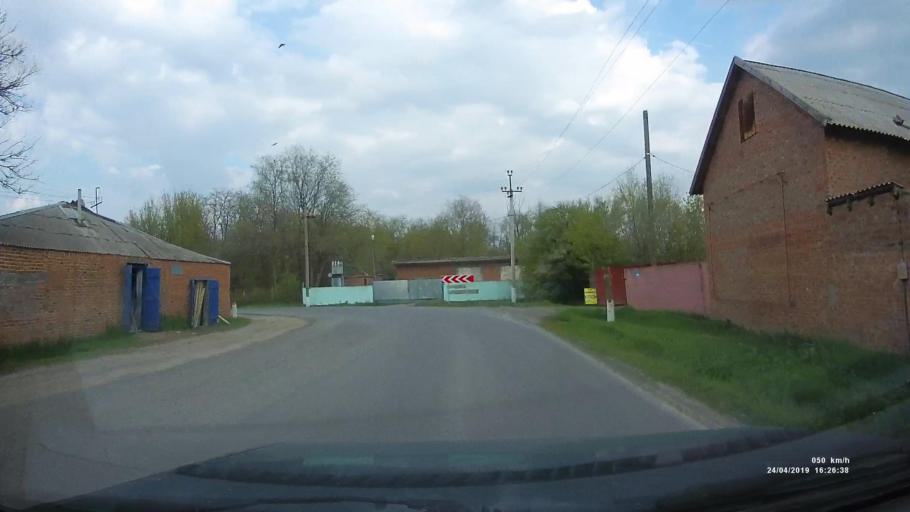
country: RU
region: Rostov
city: Orlovskiy
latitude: 46.8619
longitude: 42.0398
